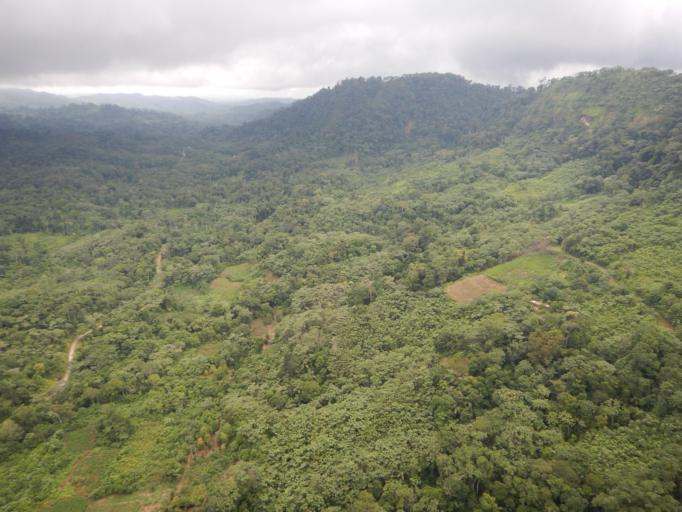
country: BO
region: Cochabamba
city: Chimore
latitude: -17.2779
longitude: -64.6091
